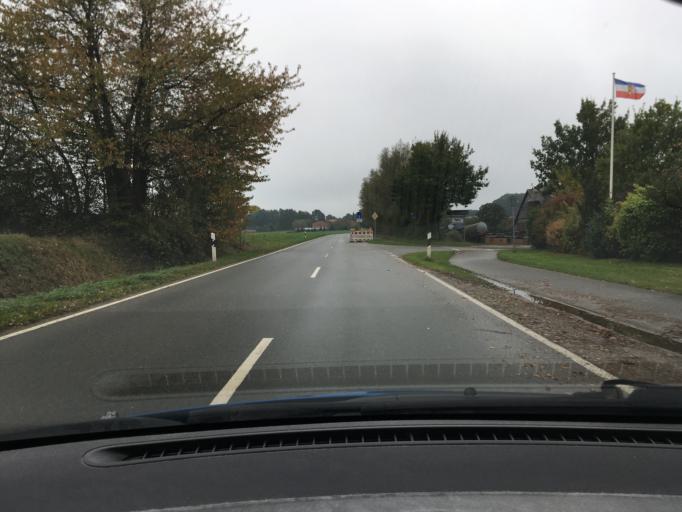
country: DE
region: Schleswig-Holstein
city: Bosdorf
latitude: 54.1155
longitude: 10.4768
